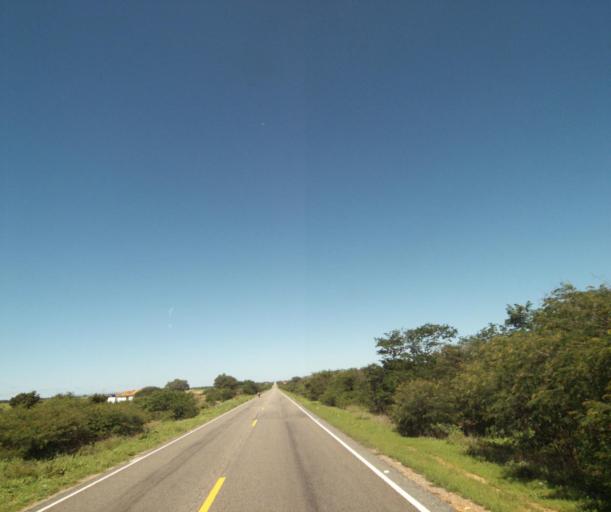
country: BR
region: Bahia
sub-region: Palmas De Monte Alto
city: Palmas de Monte Alto
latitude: -14.2539
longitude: -43.2174
